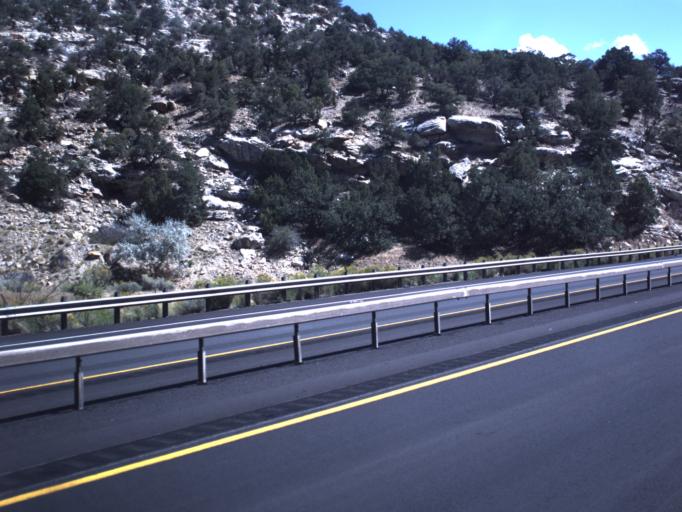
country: US
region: Utah
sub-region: Sevier County
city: Salina
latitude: 38.9079
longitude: -111.6975
